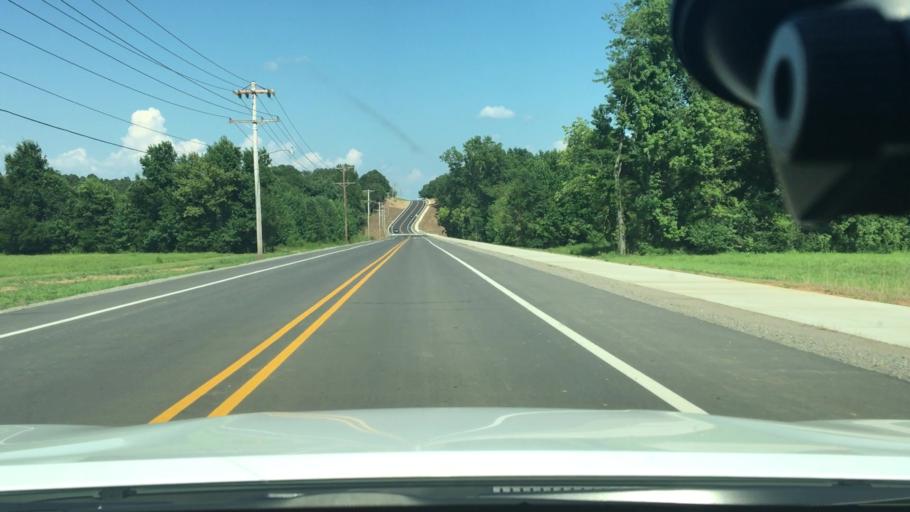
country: US
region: Arkansas
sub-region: Johnson County
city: Clarksville
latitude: 35.4620
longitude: -93.5008
